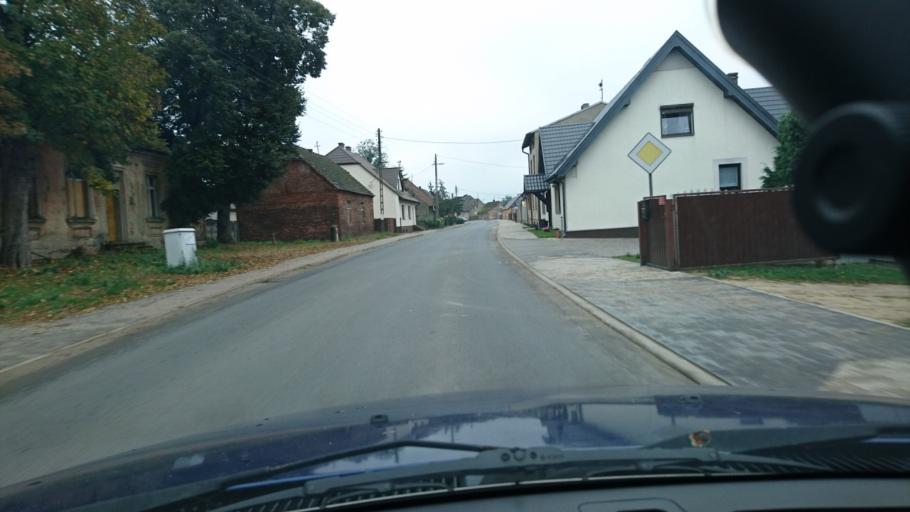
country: PL
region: Greater Poland Voivodeship
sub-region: Powiat ostrowski
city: Odolanow
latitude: 51.5741
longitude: 17.6266
